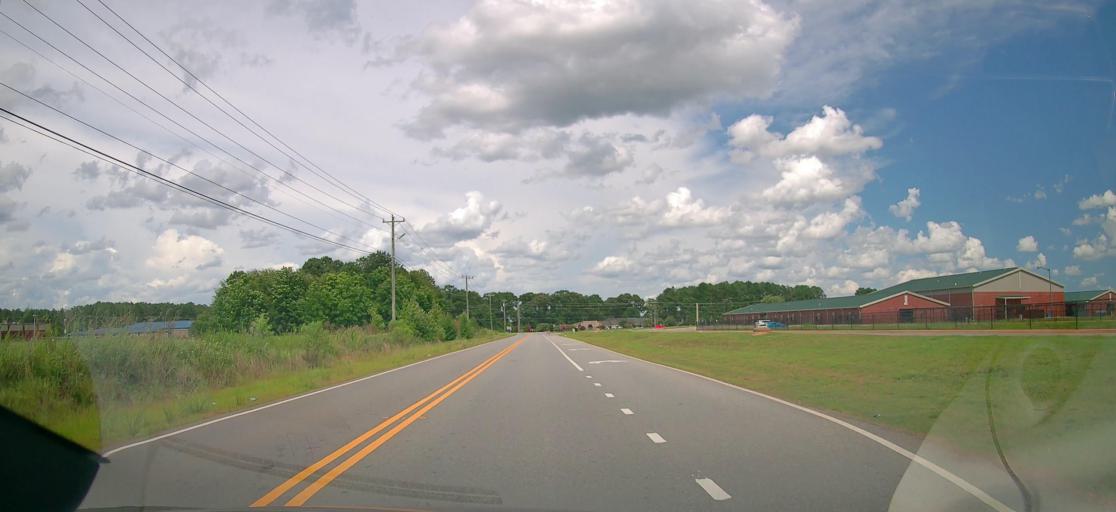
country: US
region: Georgia
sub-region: Houston County
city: Centerville
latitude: 32.5785
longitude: -83.6972
